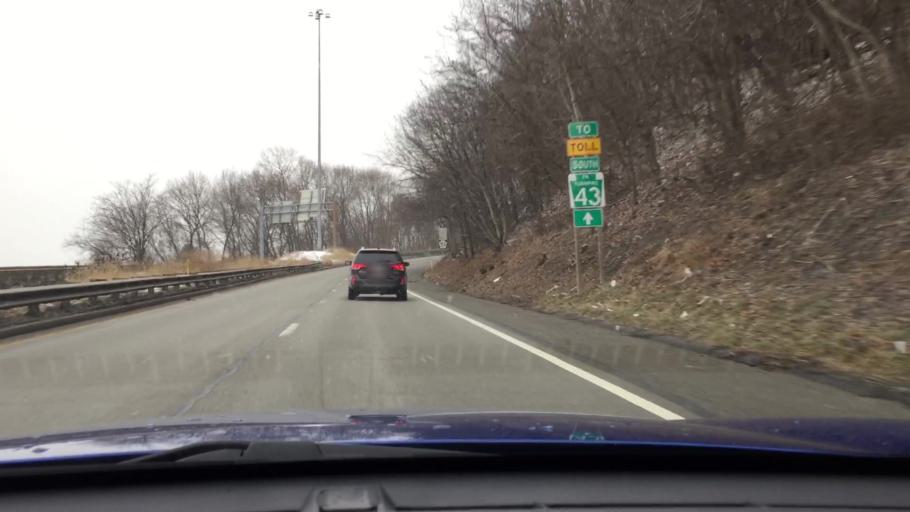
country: US
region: Pennsylvania
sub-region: Allegheny County
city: Elizabeth
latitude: 40.2750
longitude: -79.8942
